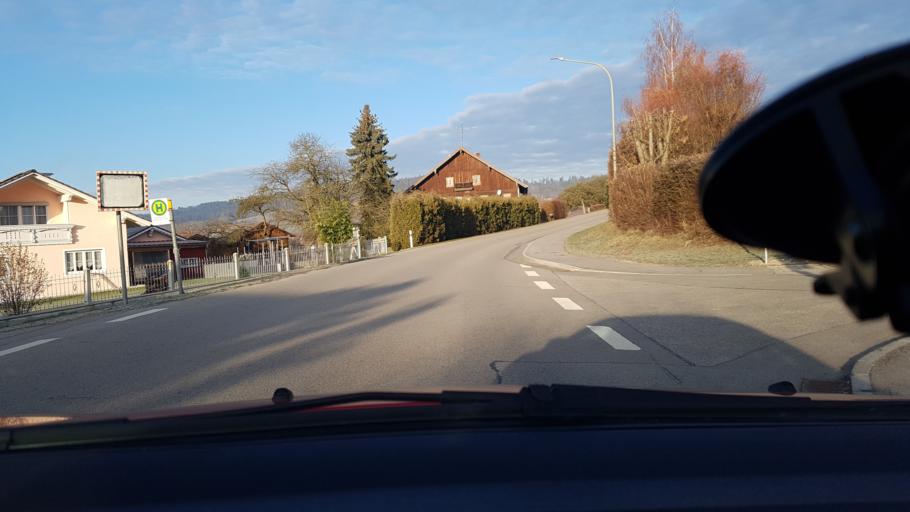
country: DE
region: Bavaria
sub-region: Lower Bavaria
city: Stubenberg
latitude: 48.3109
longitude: 13.0709
